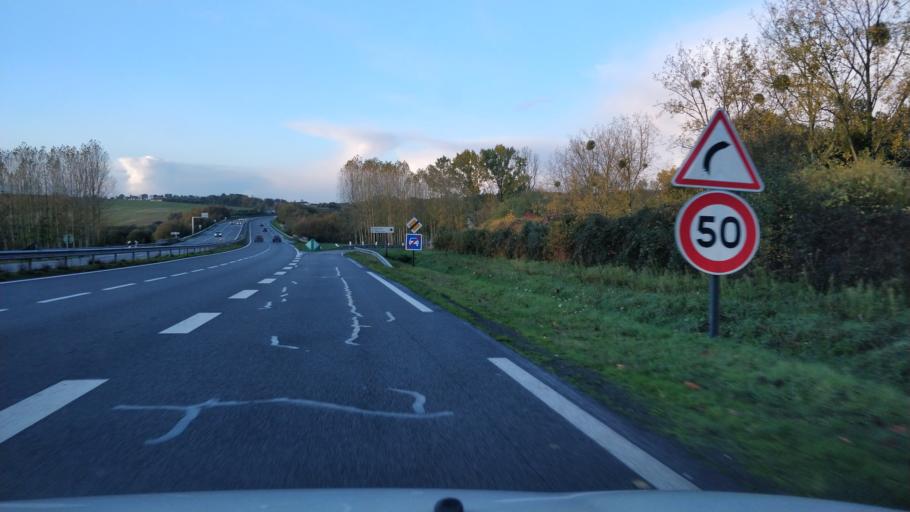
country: FR
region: Brittany
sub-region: Departement du Morbihan
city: Saint-Gonnery
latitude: 48.1373
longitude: -2.7951
